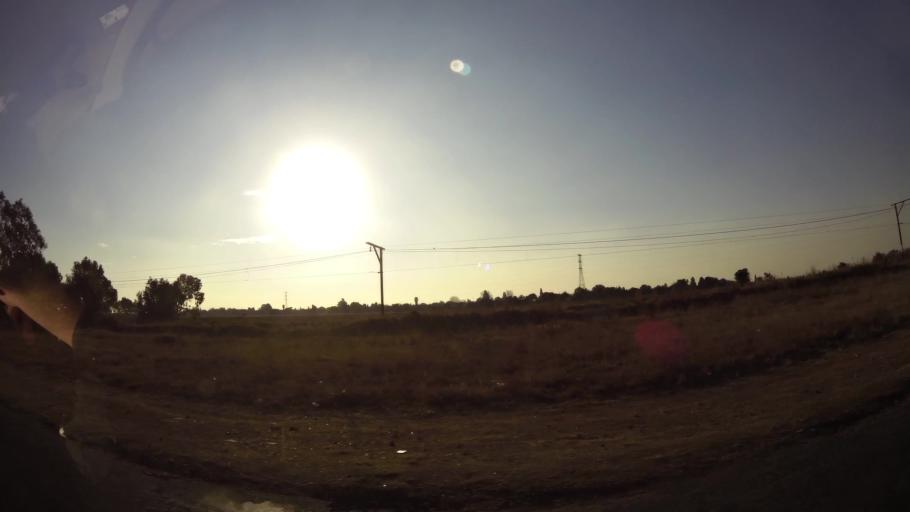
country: ZA
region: Gauteng
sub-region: West Rand District Municipality
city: Randfontein
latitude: -26.1937
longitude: 27.6826
